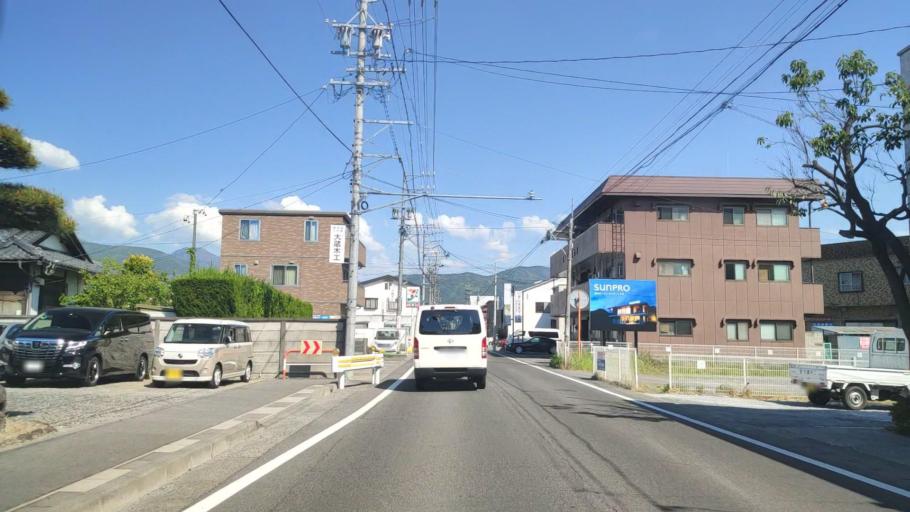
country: JP
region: Nagano
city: Matsumoto
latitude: 36.2404
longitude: 137.9592
